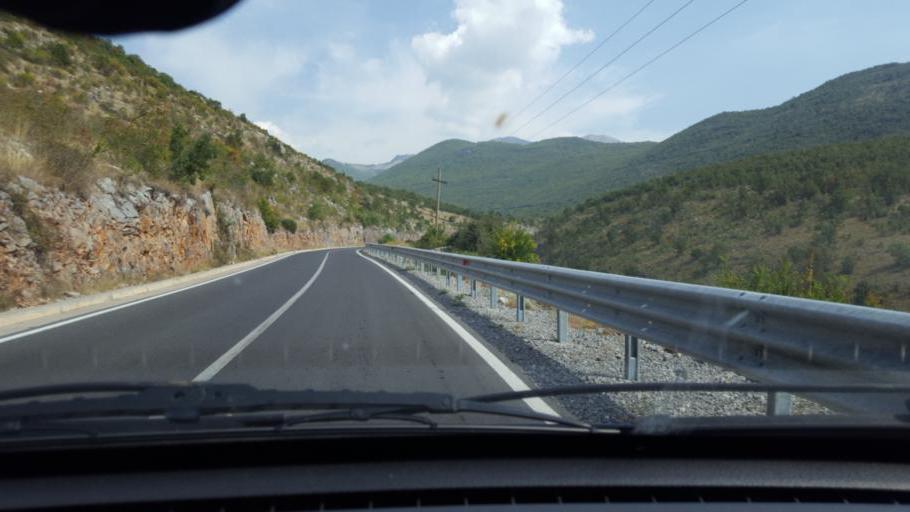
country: AL
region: Shkoder
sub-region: Rrethi i Malesia e Madhe
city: Hot
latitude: 42.3742
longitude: 19.4627
